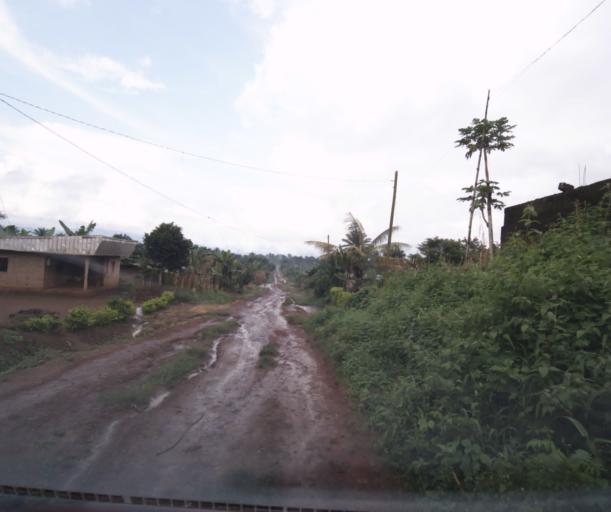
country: CM
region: Littoral
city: Melong
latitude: 5.0577
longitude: 9.9632
